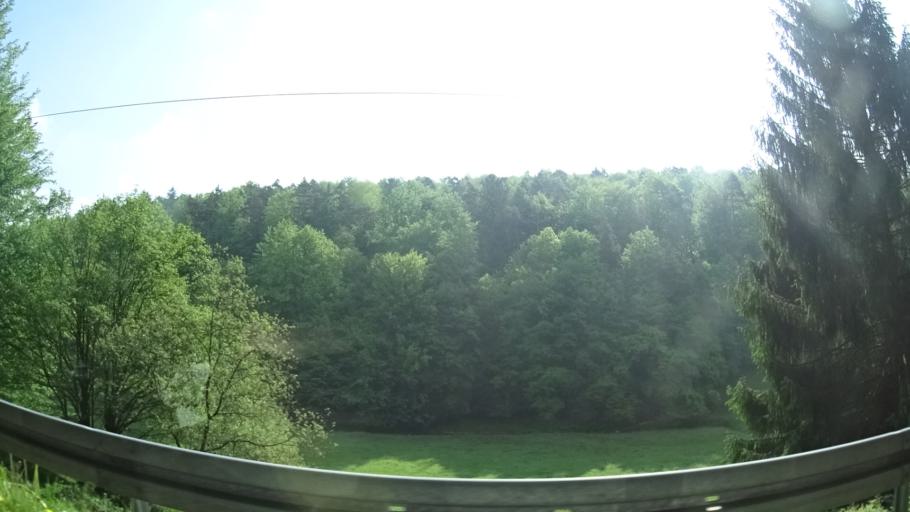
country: DE
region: Bavaria
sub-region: Regierungsbezirk Unterfranken
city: Weibersbrunn
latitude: 49.9294
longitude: 9.3982
